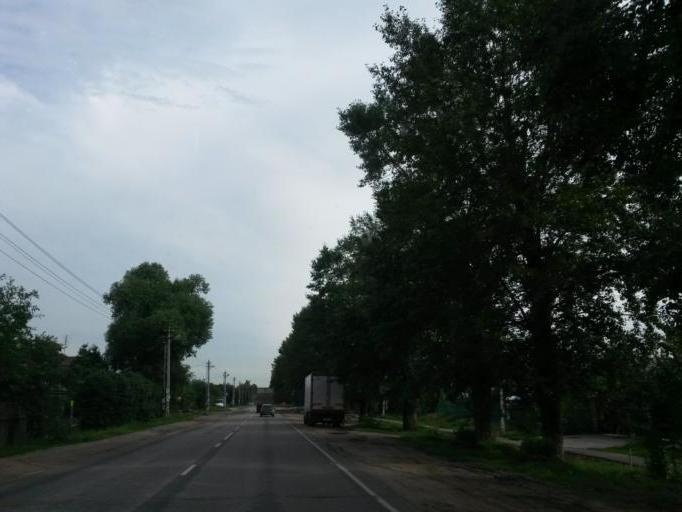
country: RU
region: Moskovskaya
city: Yam
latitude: 55.4809
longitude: 37.7515
